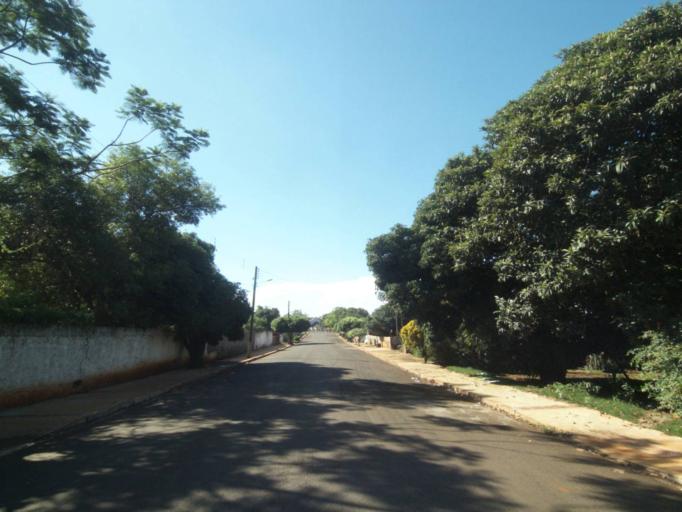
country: BR
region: Parana
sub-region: Sertanopolis
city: Sertanopolis
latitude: -23.0394
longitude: -50.8135
